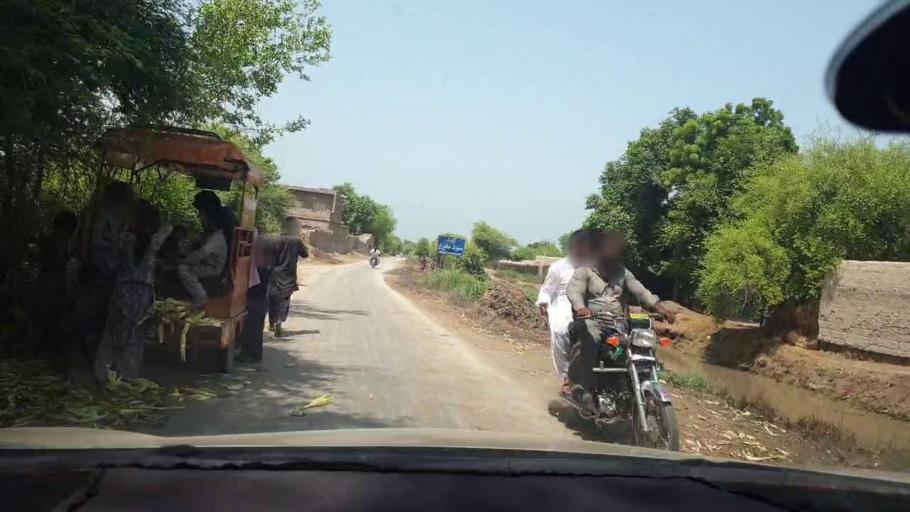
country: PK
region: Sindh
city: Kambar
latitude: 27.6500
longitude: 67.9670
